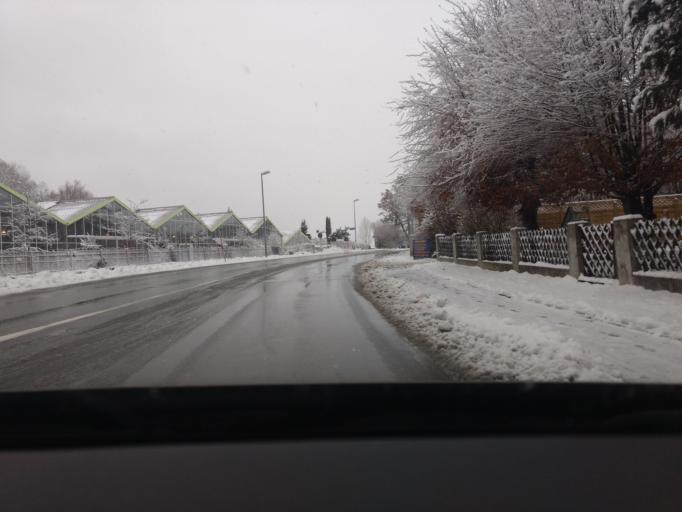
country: DE
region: Bavaria
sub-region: Upper Bavaria
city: Vachendorf
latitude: 47.8564
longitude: 12.6293
